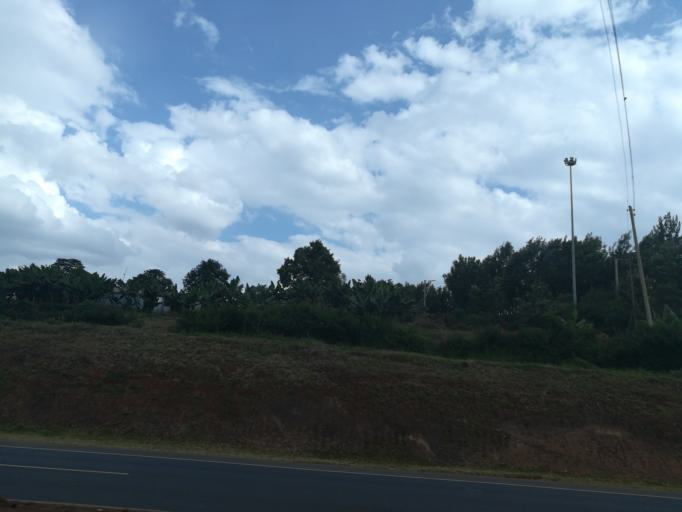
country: KE
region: Nairobi Area
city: Nairobi
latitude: -1.3173
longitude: 36.7743
